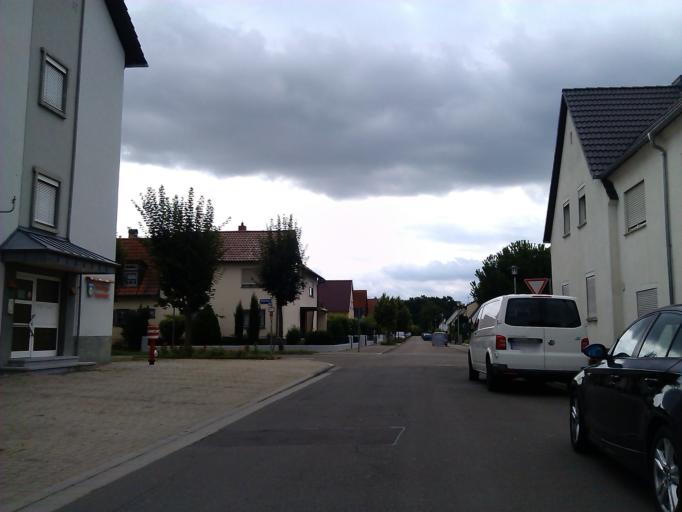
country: DE
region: Rheinland-Pfalz
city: Schifferstadt
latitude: 49.3768
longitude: 8.3849
